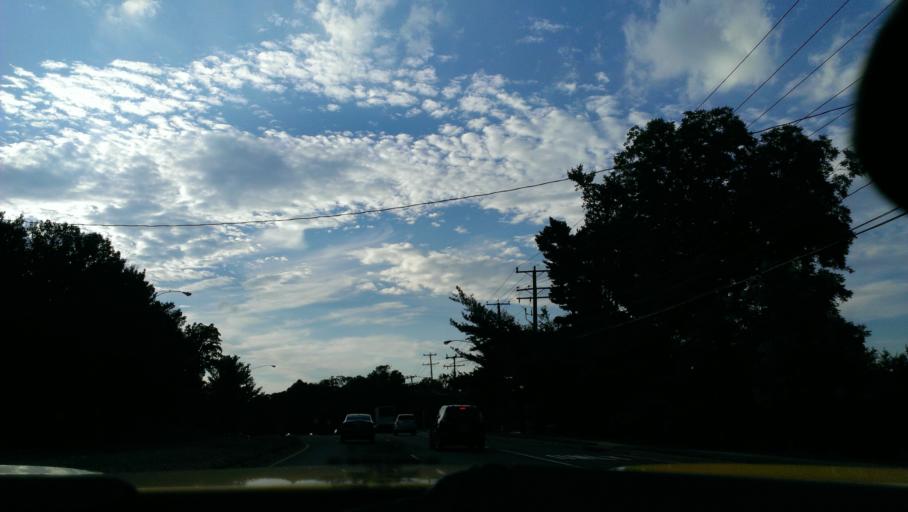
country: US
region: Virginia
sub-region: Fairfax County
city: Pimmit Hills
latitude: 38.9050
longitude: -77.2055
